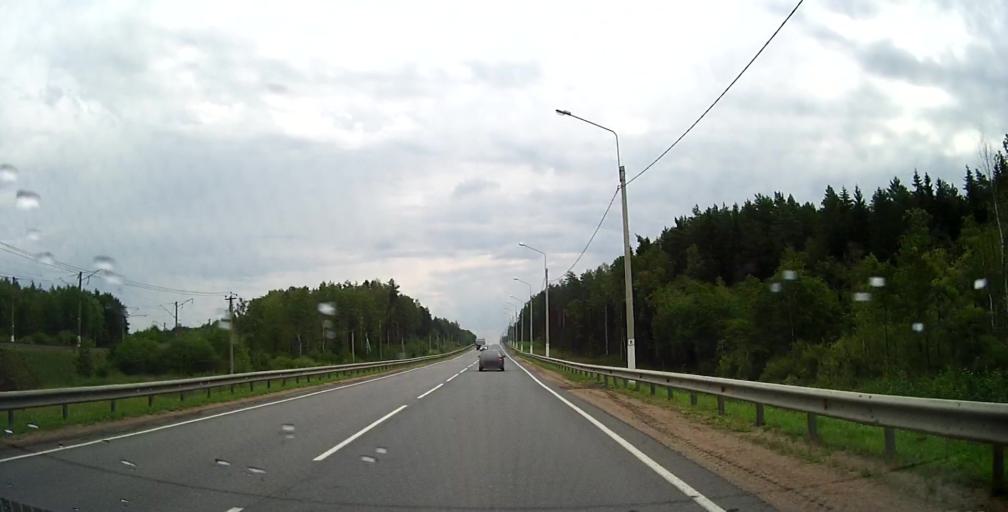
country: RU
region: Smolensk
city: Katyn'
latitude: 54.7721
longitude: 31.7687
